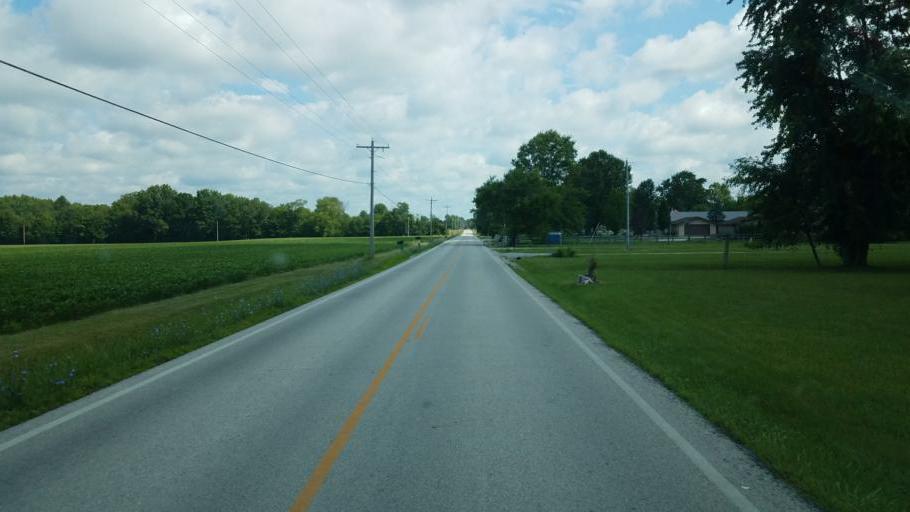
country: US
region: Ohio
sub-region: Delaware County
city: Ashley
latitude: 40.3184
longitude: -82.9328
